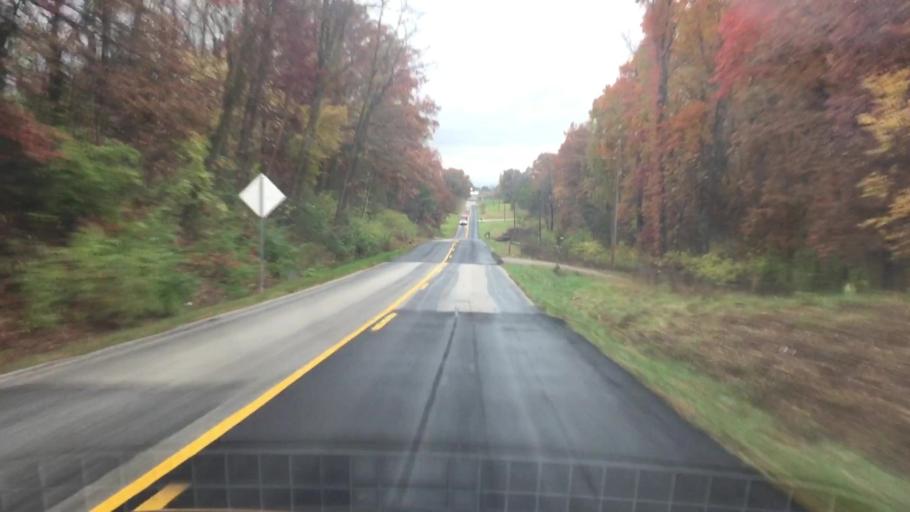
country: US
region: Missouri
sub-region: Boone County
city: Columbia
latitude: 38.9639
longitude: -92.4957
